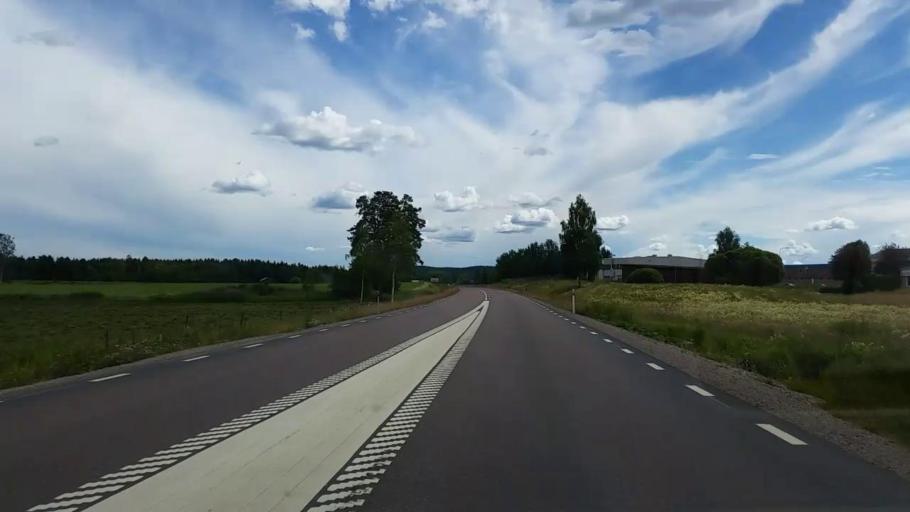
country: SE
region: Gaevleborg
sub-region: Ovanakers Kommun
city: Edsbyn
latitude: 61.3760
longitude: 15.8404
